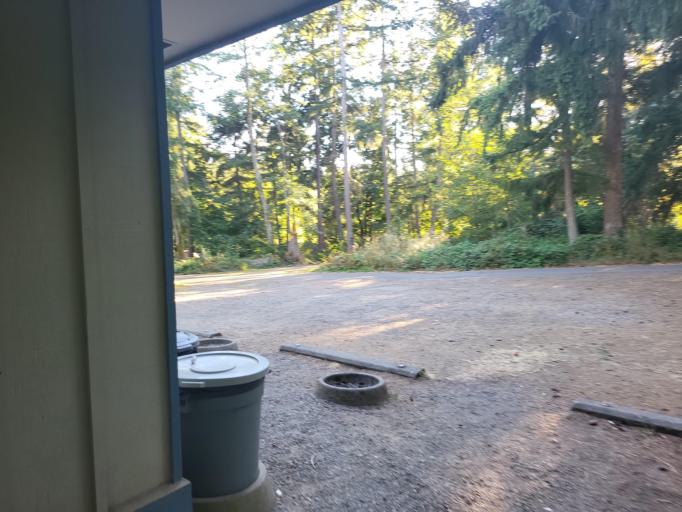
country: US
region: Washington
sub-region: Pierce County
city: Tacoma
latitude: 47.3149
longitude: -122.4047
